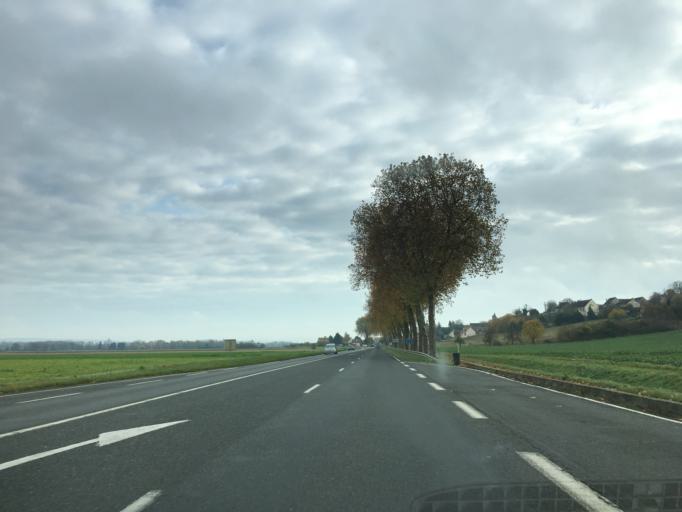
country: FR
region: Bourgogne
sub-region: Departement de l'Yonne
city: Courlon-sur-Yonne
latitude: 48.3053
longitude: 3.1717
